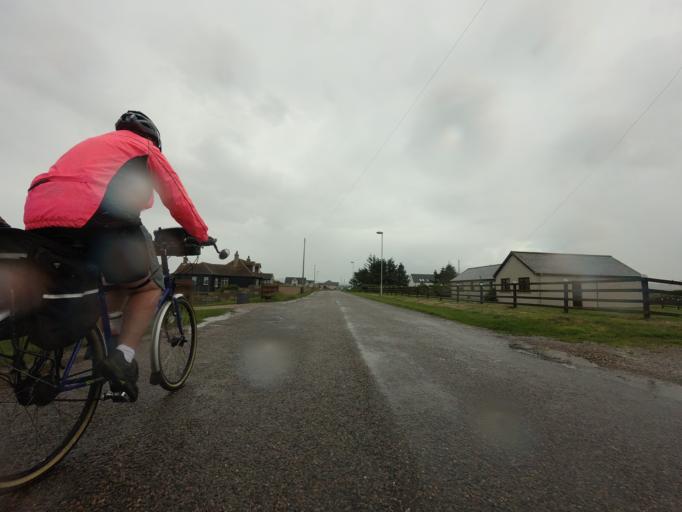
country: GB
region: Scotland
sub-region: Moray
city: Fochabers
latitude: 57.6724
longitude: -3.0859
